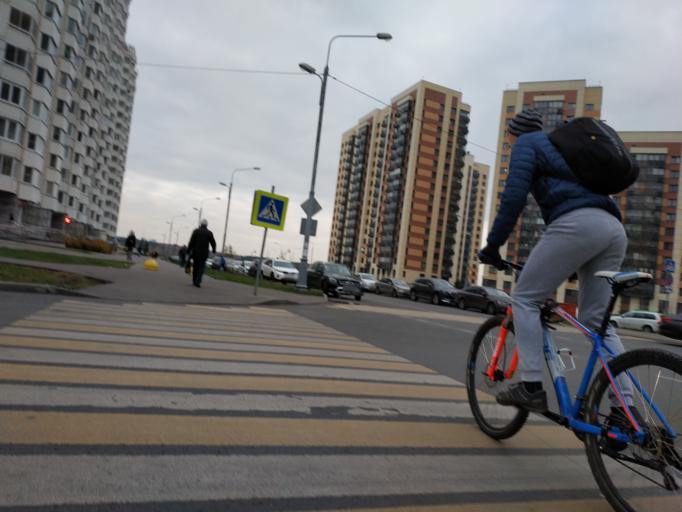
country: RU
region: Moscow
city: Novo-Peredelkino
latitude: 55.6371
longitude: 37.3272
